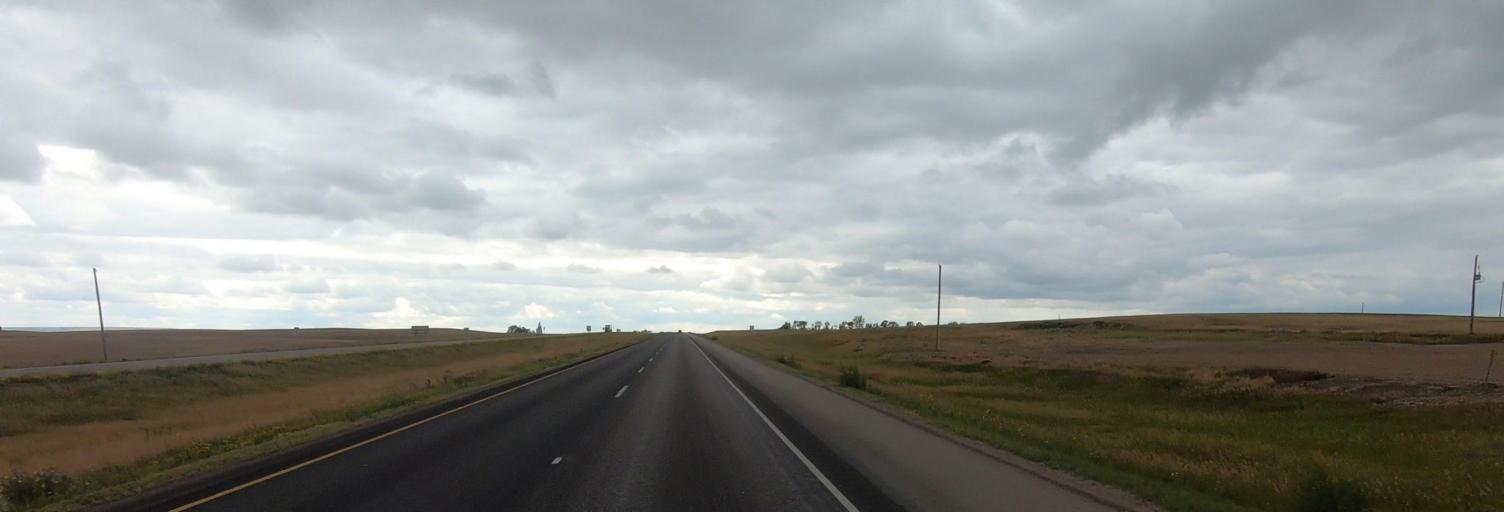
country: CA
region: Saskatchewan
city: Shaunavon
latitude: 50.0982
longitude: -108.4971
